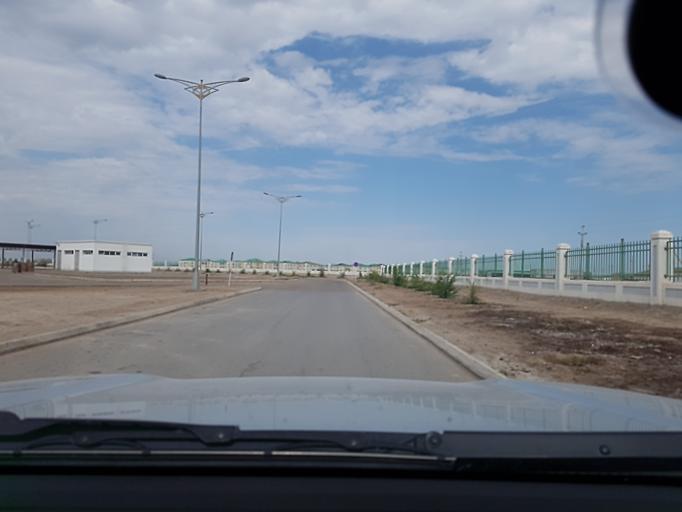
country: TM
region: Dasoguz
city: Dasoguz
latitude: 41.8809
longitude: 59.9510
